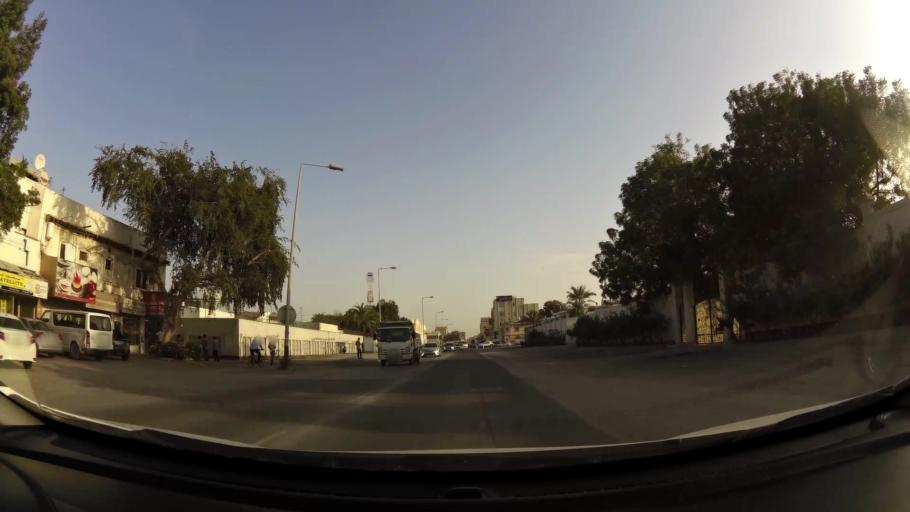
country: BH
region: Manama
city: Jidd Hafs
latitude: 26.1978
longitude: 50.4857
